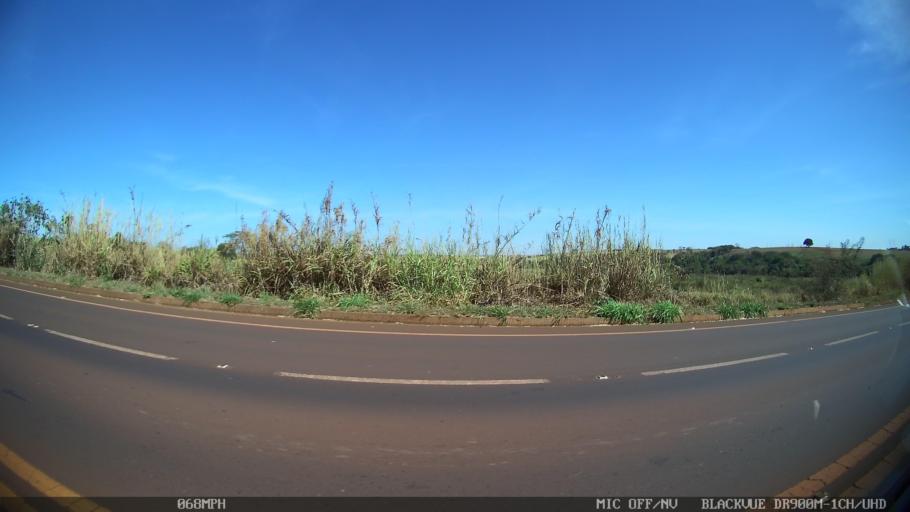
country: BR
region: Sao Paulo
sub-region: Sao Joaquim Da Barra
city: Sao Joaquim da Barra
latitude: -20.5322
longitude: -47.8304
